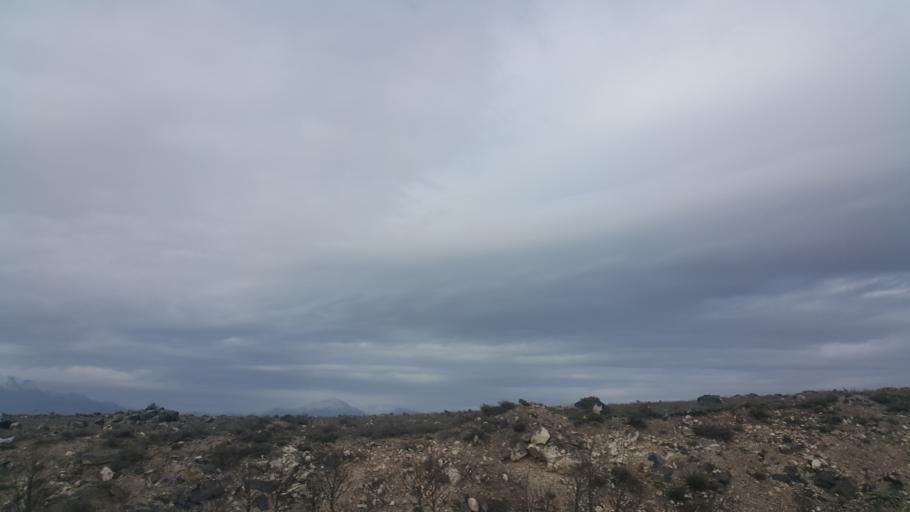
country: TR
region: Konya
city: Beyviran
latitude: 37.9257
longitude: 34.1093
